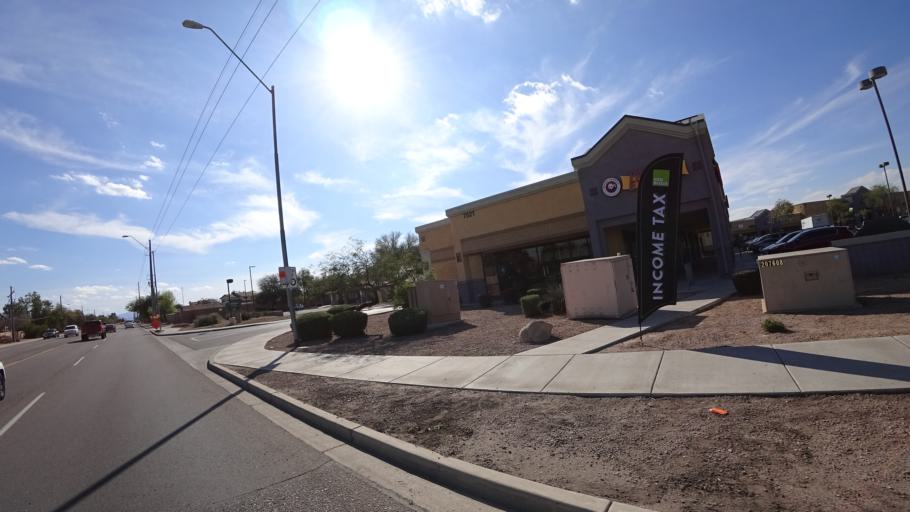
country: US
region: Arizona
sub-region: Maricopa County
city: Peoria
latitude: 33.5945
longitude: -112.2203
